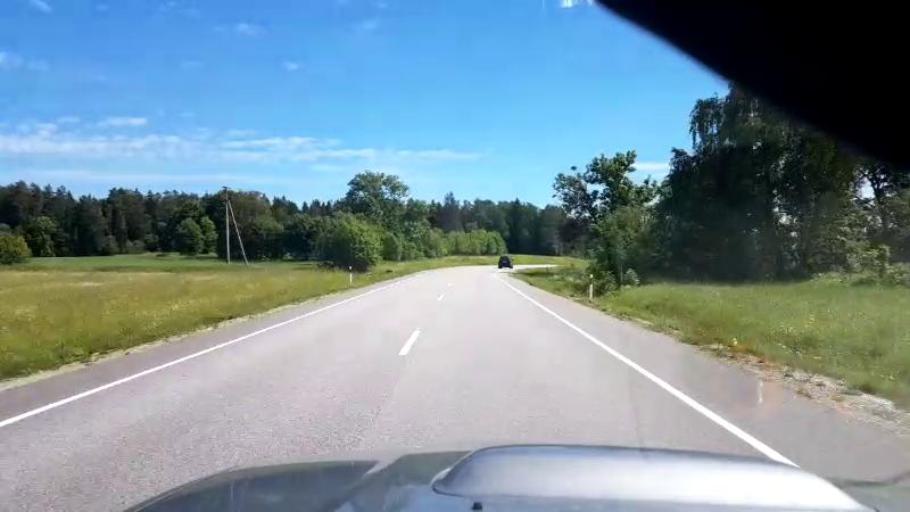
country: EE
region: Jaervamaa
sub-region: Jaerva-Jaani vald
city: Jarva-Jaani
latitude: 59.0139
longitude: 25.9170
